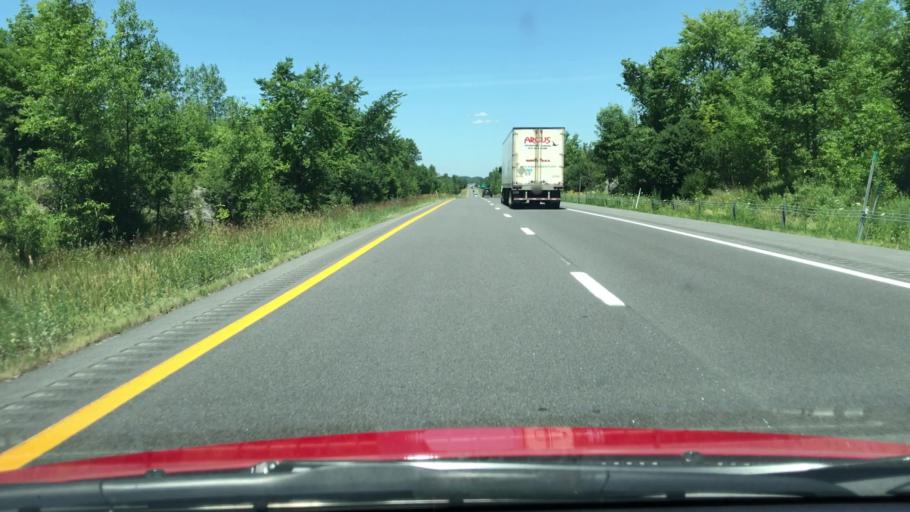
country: US
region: New York
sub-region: Clinton County
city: Cumberland Head
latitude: 44.7536
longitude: -73.4280
